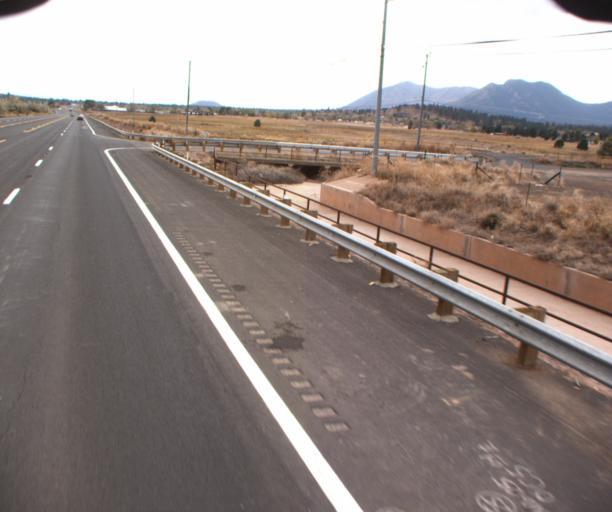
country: US
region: Arizona
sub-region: Coconino County
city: Flagstaff
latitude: 35.3211
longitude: -111.5428
